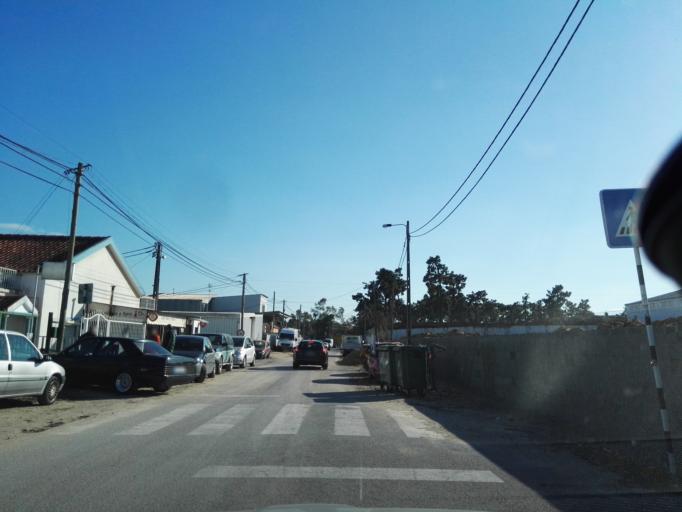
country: PT
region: Setubal
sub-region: Seixal
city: Corroios
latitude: 38.6284
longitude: -9.1457
